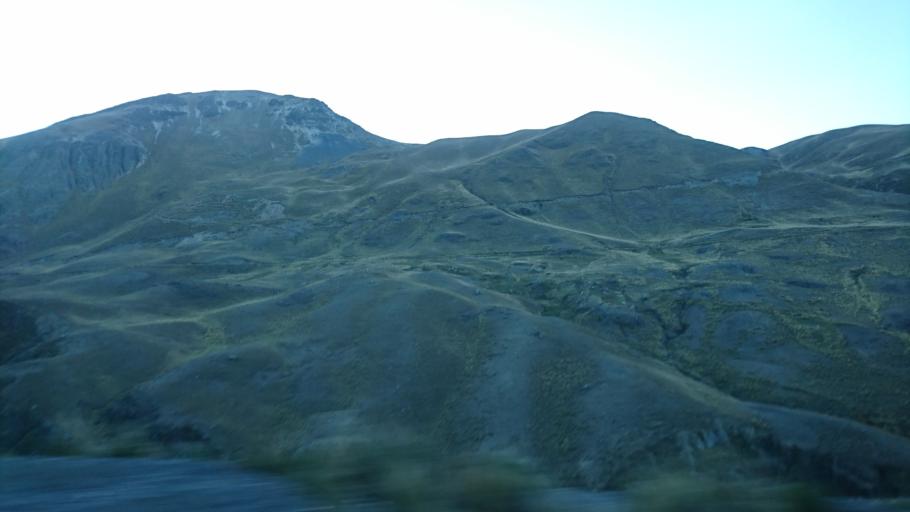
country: BO
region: La Paz
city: La Paz
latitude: -16.4144
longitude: -68.0531
